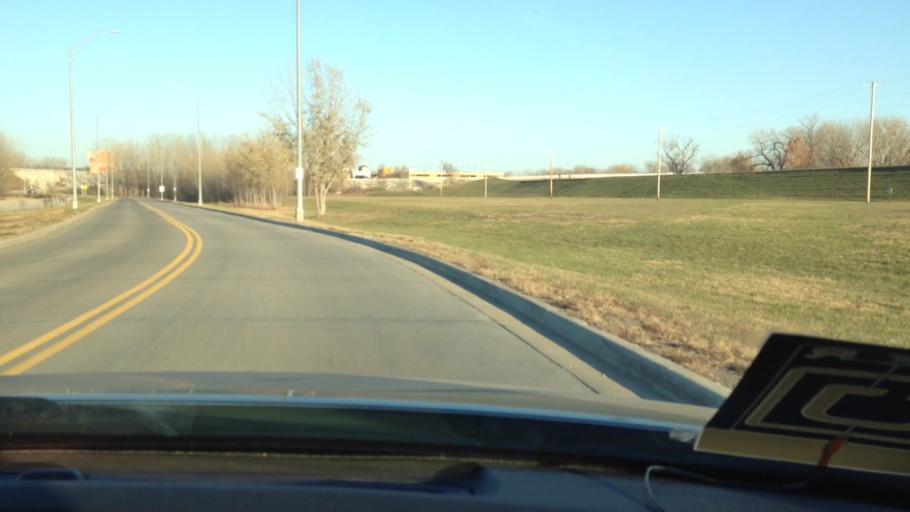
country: US
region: Missouri
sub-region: Platte County
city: Riverside
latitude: 39.1597
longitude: -94.6313
